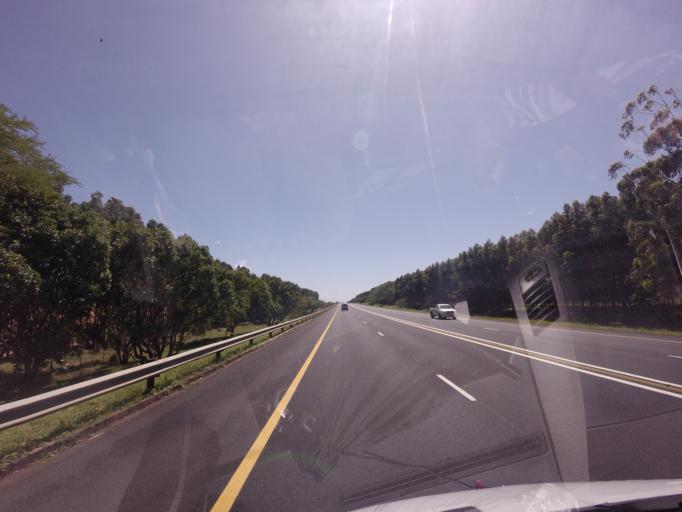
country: ZA
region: KwaZulu-Natal
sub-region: uThungulu District Municipality
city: Eshowe
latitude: -29.0014
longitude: 31.6888
